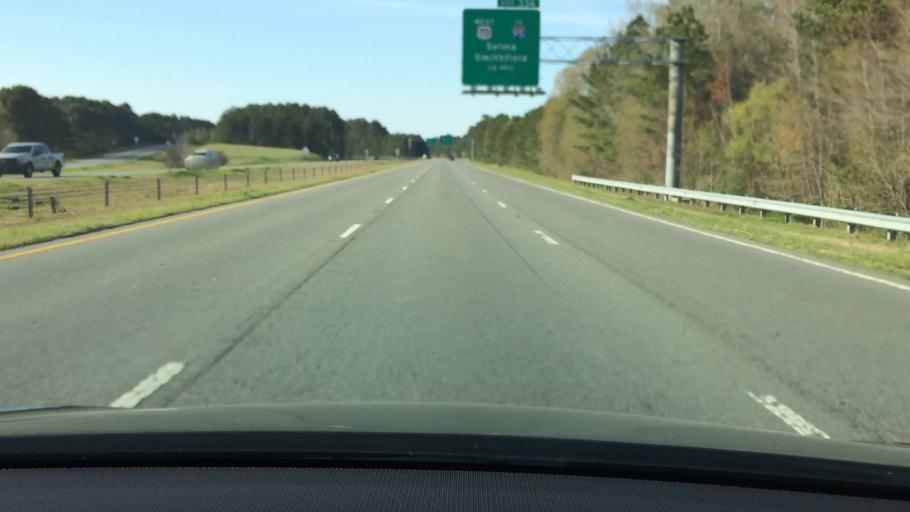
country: US
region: North Carolina
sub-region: Johnston County
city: Selma
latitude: 35.5052
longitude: -78.2810
